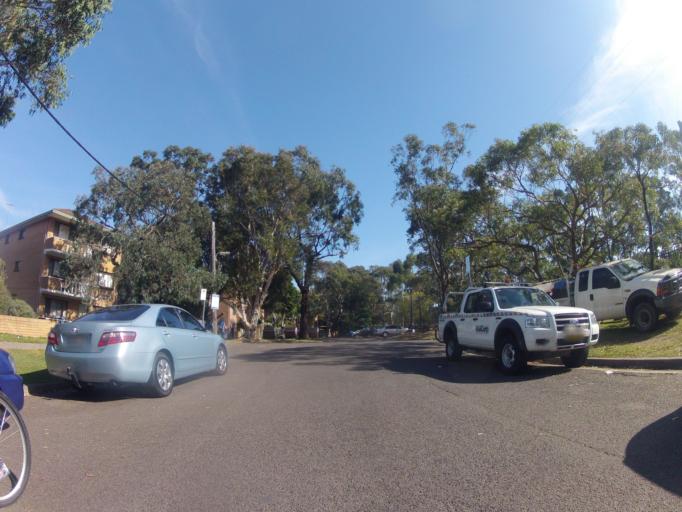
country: AU
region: New South Wales
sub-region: Sutherland Shire
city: Caringbah
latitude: -34.0411
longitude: 151.1183
